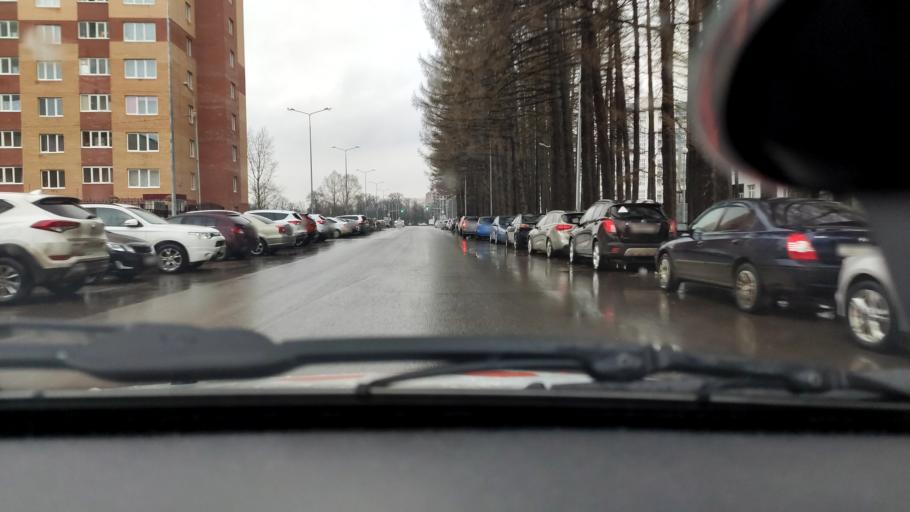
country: RU
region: Bashkortostan
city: Mikhaylovka
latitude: 54.7915
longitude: 55.8545
